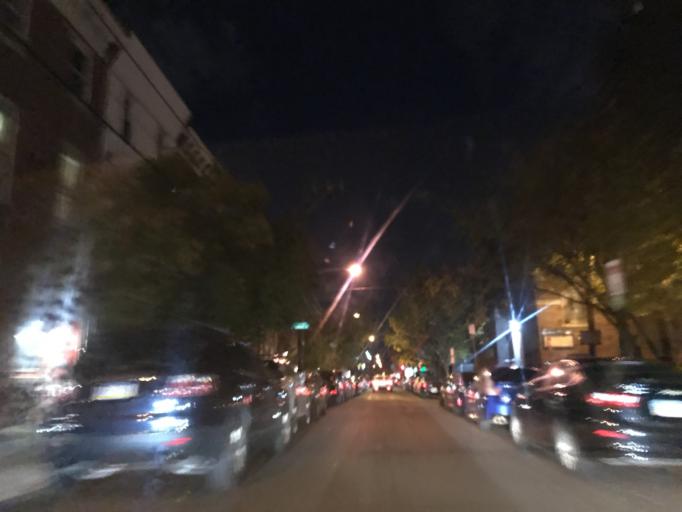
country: US
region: Pennsylvania
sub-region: Philadelphia County
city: Philadelphia
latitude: 39.9381
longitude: -75.1597
